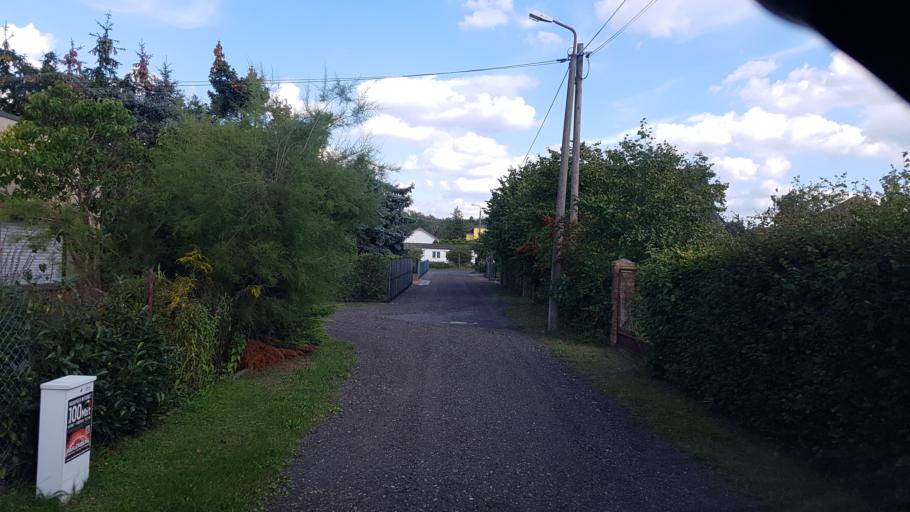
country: DE
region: Brandenburg
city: Tschernitz
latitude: 51.6034
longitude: 14.5836
